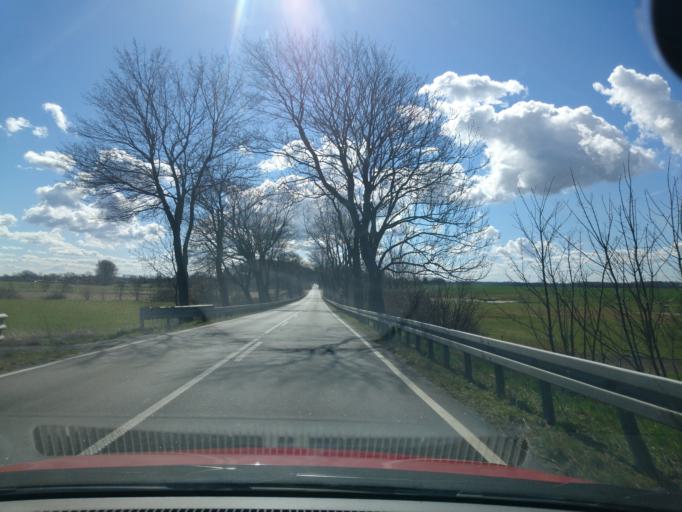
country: DE
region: Mecklenburg-Vorpommern
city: Barth
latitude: 54.3045
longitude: 12.7181
